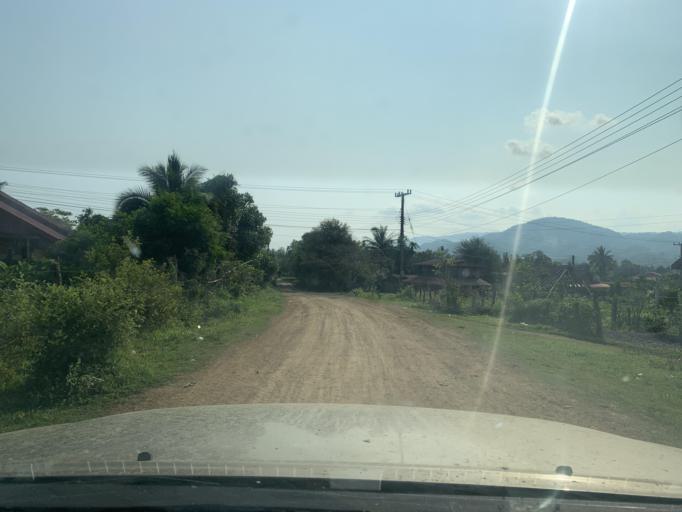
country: TH
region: Uttaradit
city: Ban Khok
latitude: 18.2820
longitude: 101.3146
